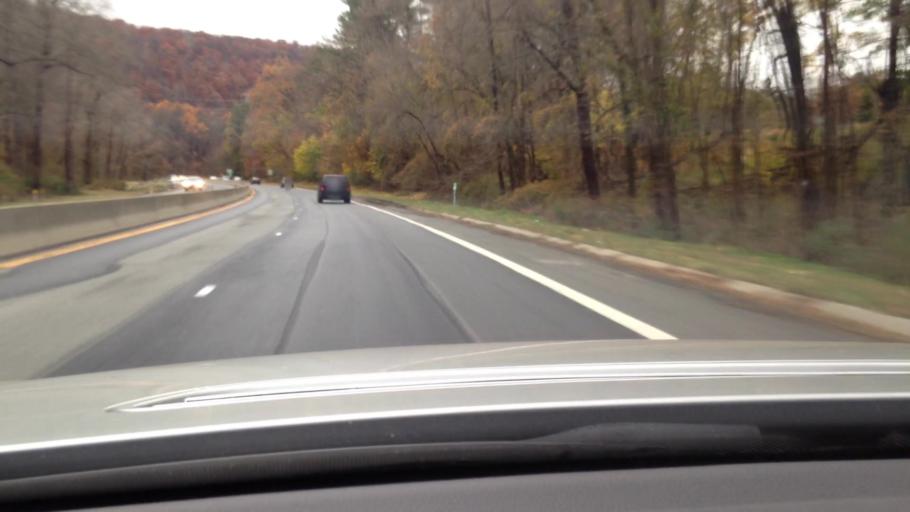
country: US
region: New York
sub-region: Westchester County
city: Hawthorne
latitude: 41.0992
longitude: -73.8108
